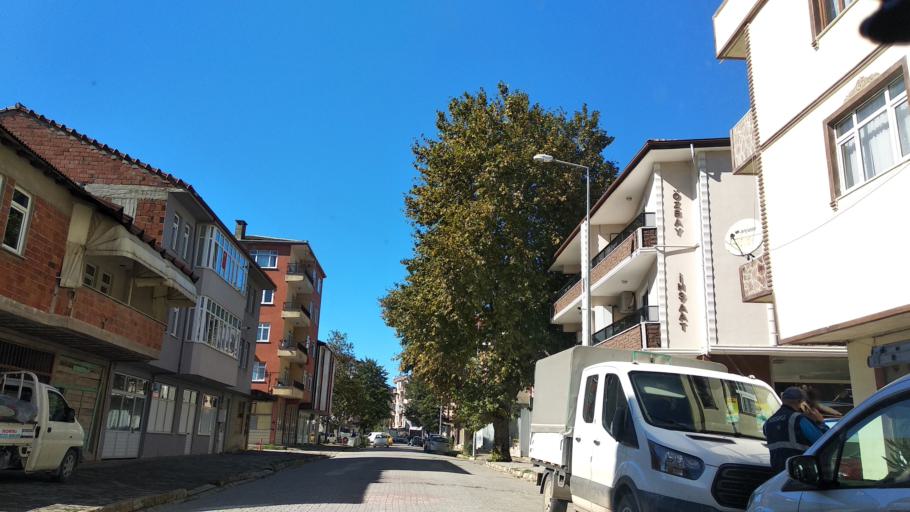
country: TR
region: Sakarya
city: Karasu
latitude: 41.0922
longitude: 30.6957
